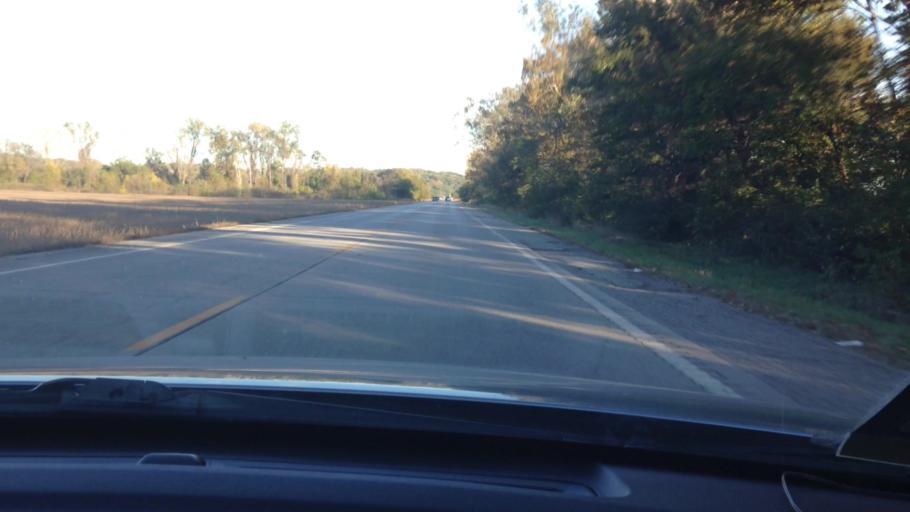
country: US
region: Kansas
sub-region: Leavenworth County
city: Leavenworth
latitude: 39.3281
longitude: -94.8809
